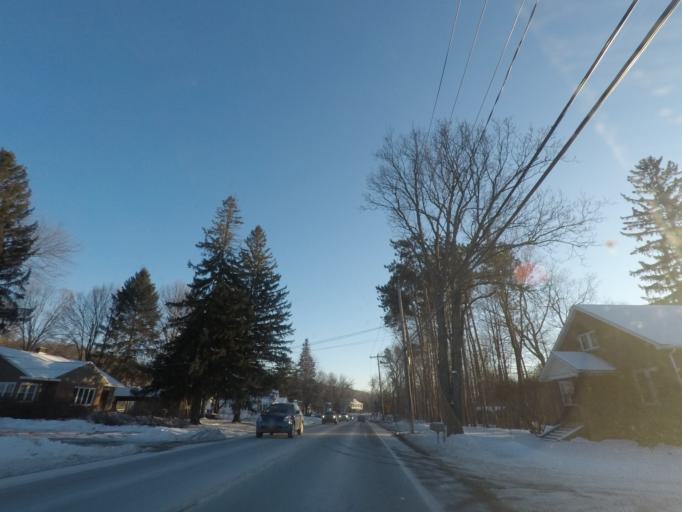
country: US
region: New York
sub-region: Saratoga County
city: Waterford
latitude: 42.8069
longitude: -73.6342
